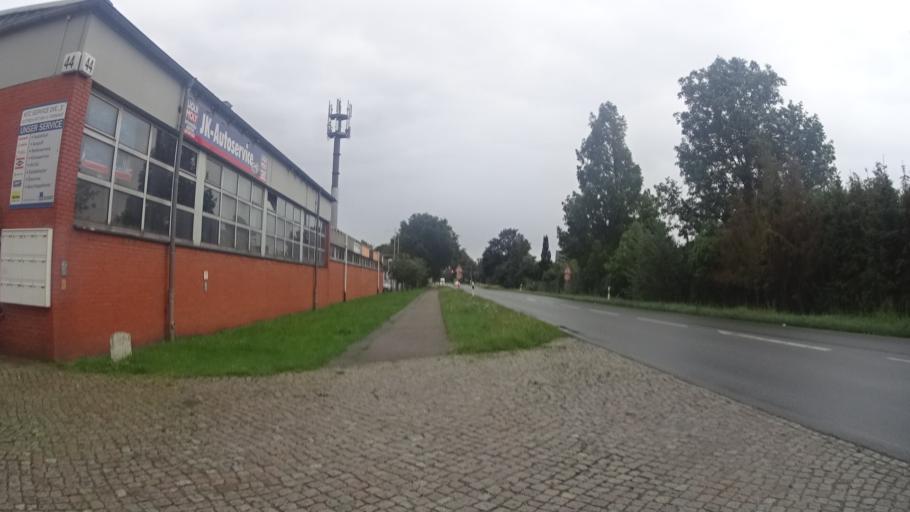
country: DE
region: Schleswig-Holstein
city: Kolln-Reisiek
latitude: 53.7673
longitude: 9.6762
